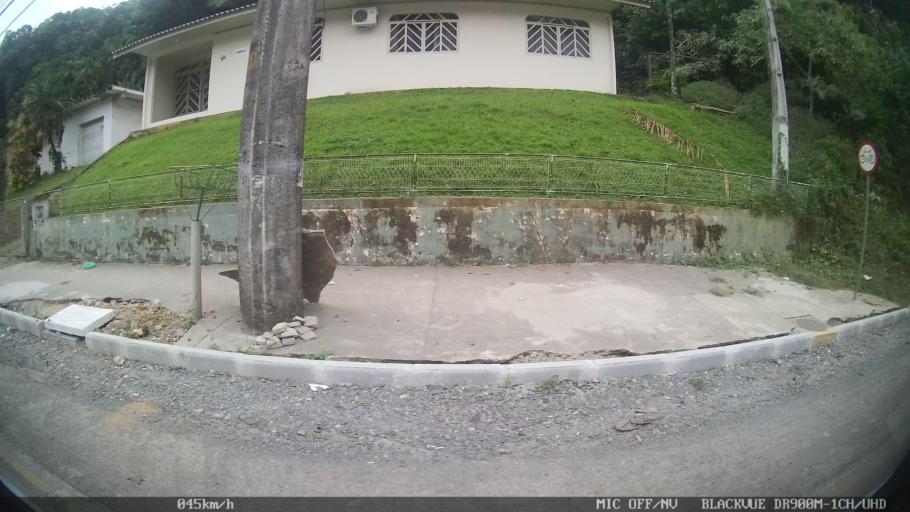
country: BR
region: Santa Catarina
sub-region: Joinville
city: Joinville
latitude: -26.3071
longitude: -48.8350
